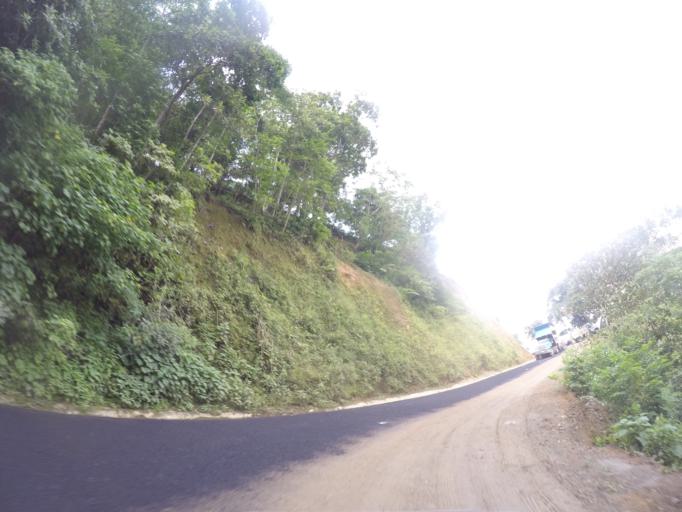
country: MX
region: Oaxaca
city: Pluma Hidalgo
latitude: 15.9461
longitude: -96.4398
